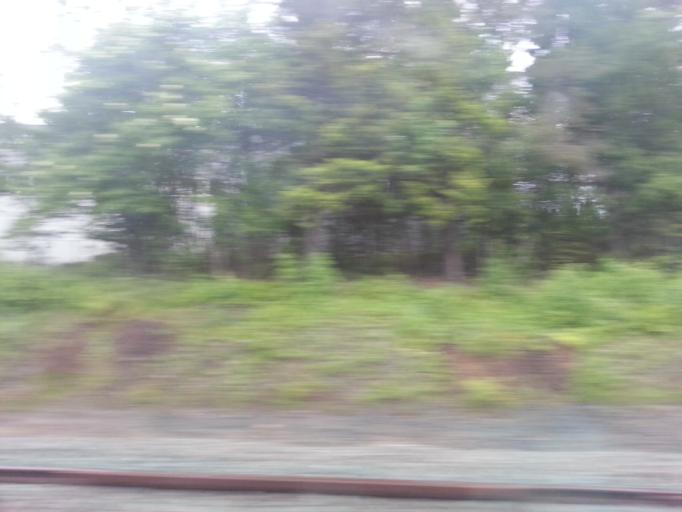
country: NO
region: Sor-Trondelag
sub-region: Trondheim
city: Trondheim
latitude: 63.3493
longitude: 10.3568
